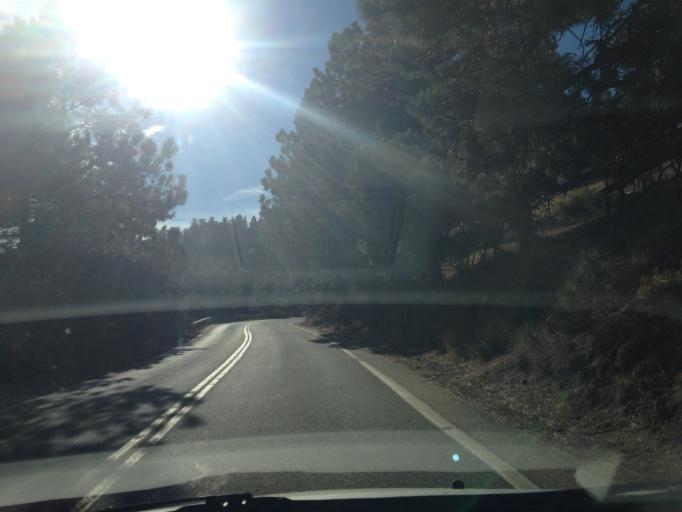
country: US
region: Colorado
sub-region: Boulder County
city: Boulder
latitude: 40.0058
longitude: -105.2949
